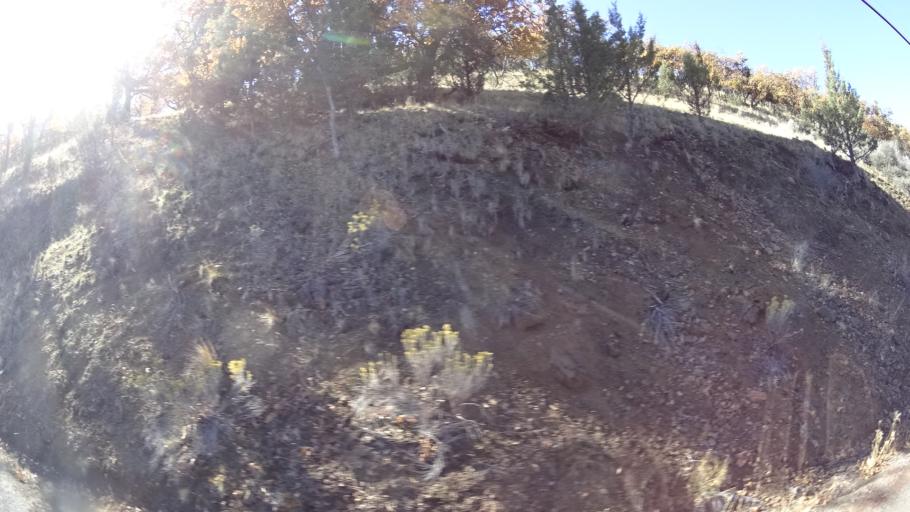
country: US
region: California
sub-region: Siskiyou County
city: Montague
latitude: 41.9777
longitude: -122.3044
